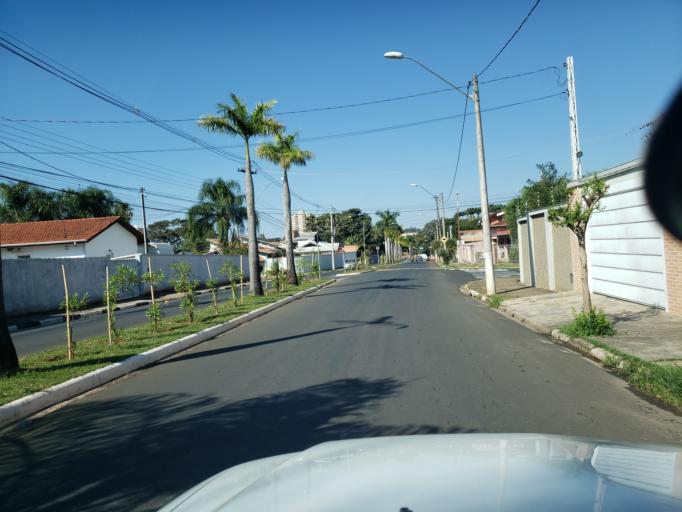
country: BR
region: Sao Paulo
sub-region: Itapira
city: Itapira
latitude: -22.4270
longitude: -46.8365
